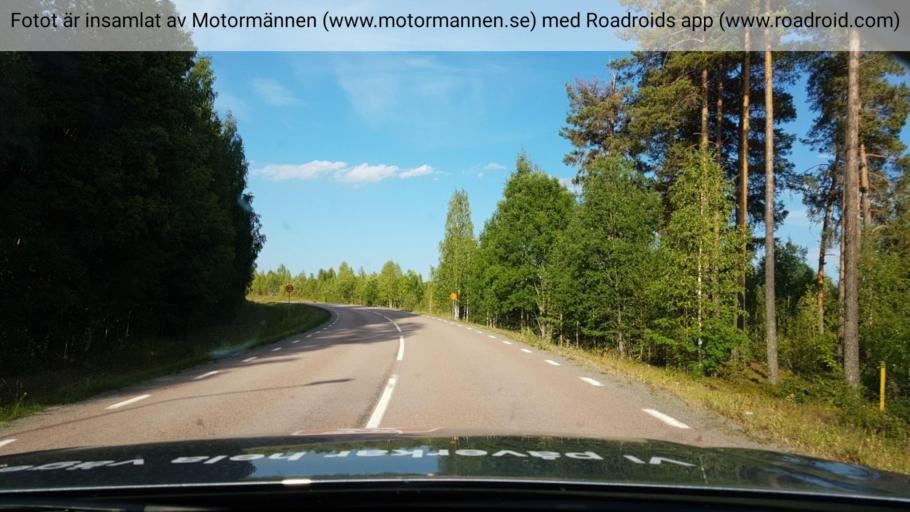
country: SE
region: Vaesternorrland
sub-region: Solleftea Kommun
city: As
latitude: 63.5921
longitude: 16.1921
